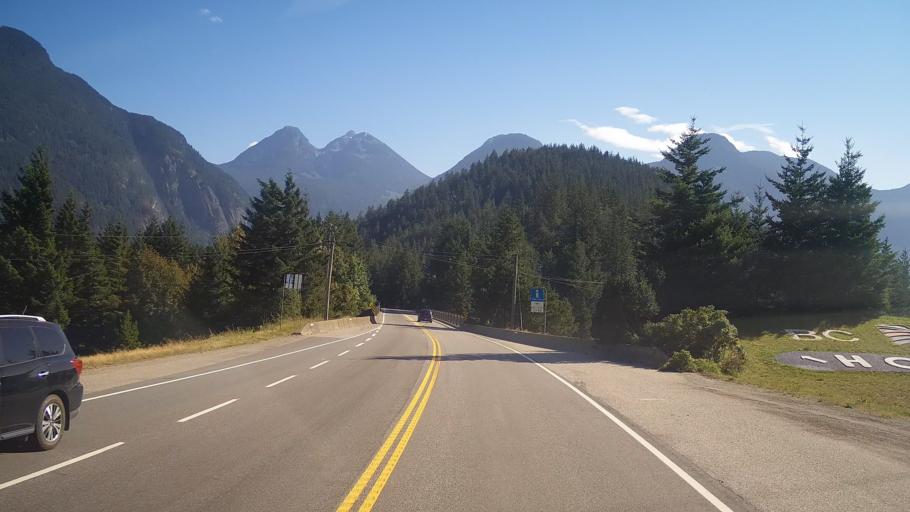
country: CA
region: British Columbia
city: Hope
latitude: 49.3915
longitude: -121.4606
